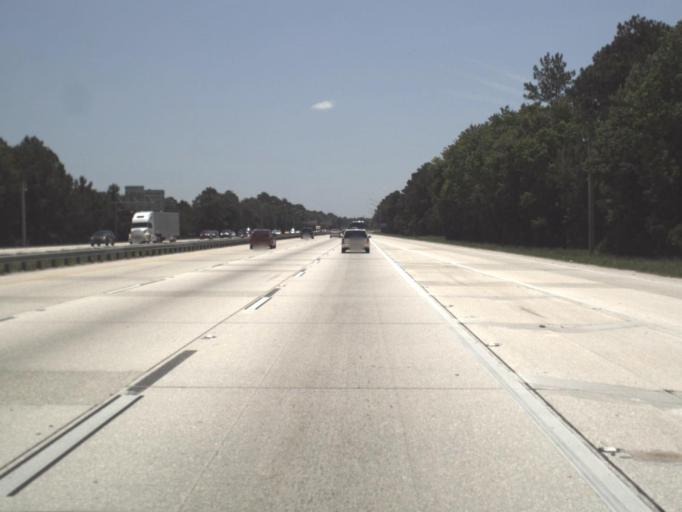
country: US
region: Florida
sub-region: Duval County
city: Jacksonville
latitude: 30.2453
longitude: -81.5903
